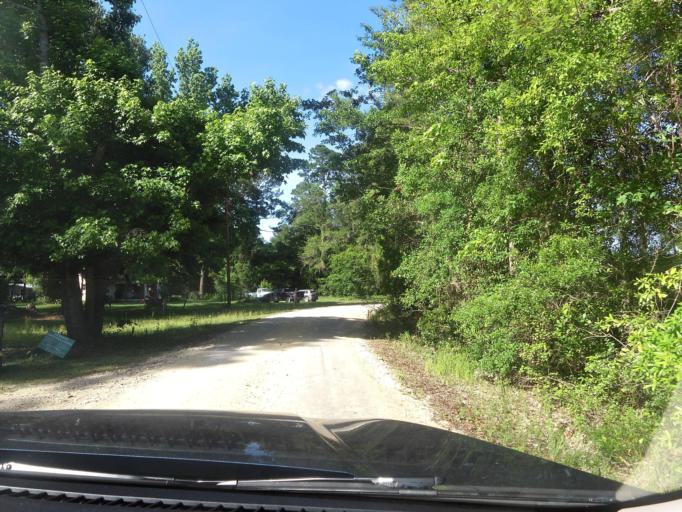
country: US
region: Florida
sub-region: Nassau County
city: Callahan
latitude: 30.5763
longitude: -81.7735
